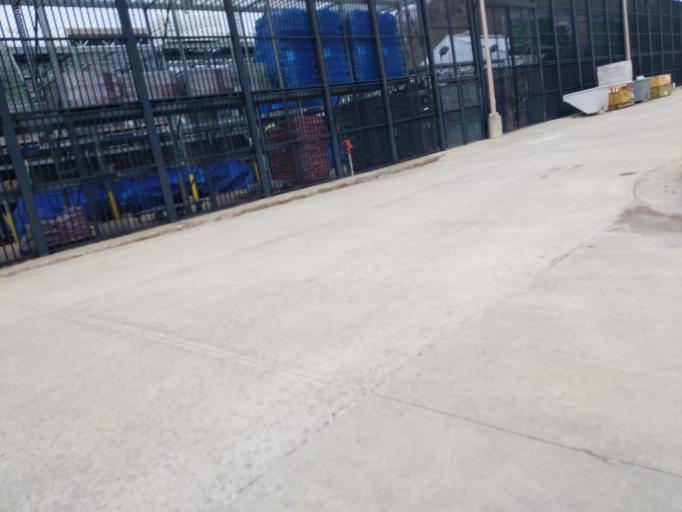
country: US
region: Ohio
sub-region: Athens County
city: Athens
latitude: 39.3348
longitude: -82.0585
